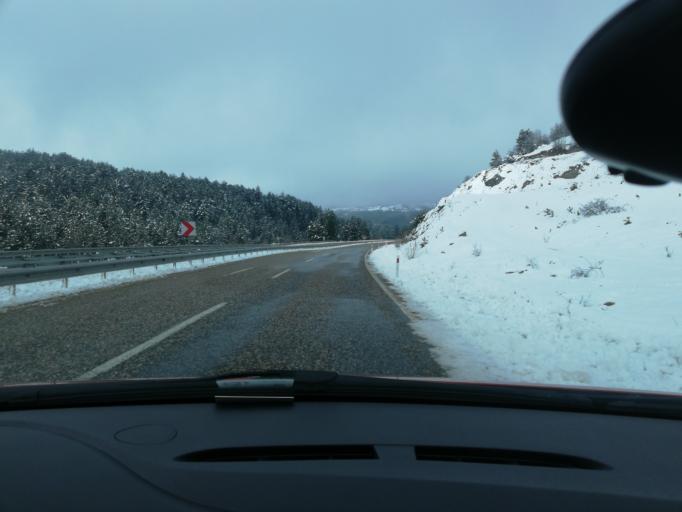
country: TR
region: Kastamonu
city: Akkaya
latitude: 41.2813
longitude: 33.4599
